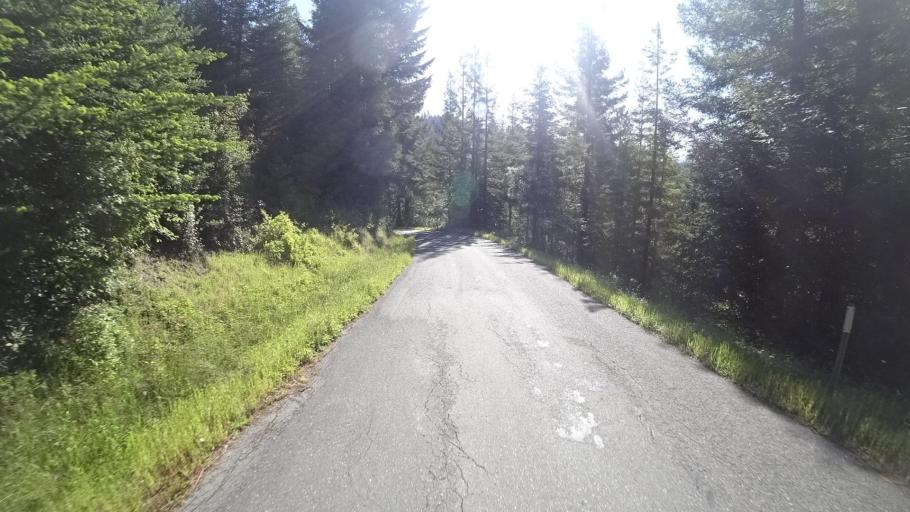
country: US
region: California
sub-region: Humboldt County
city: Rio Dell
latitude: 40.4426
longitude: -123.9708
